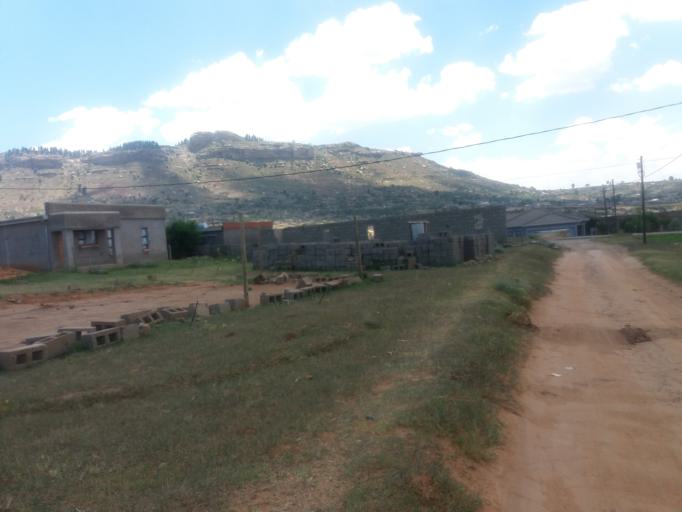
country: LS
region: Maseru
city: Maseru
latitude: -29.3673
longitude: 27.4755
